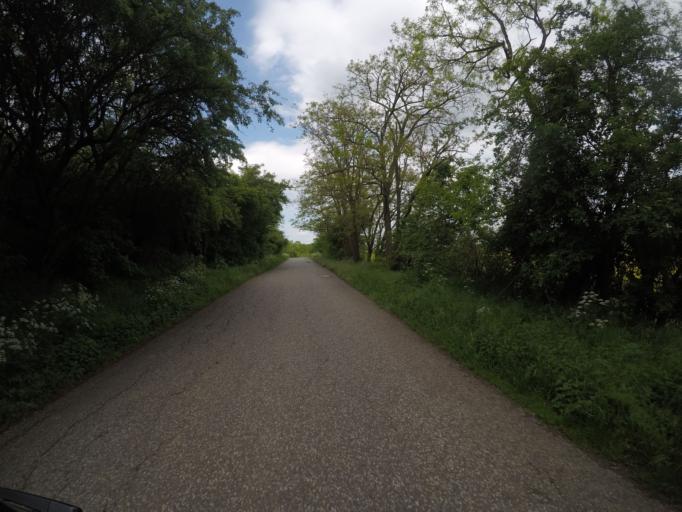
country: SK
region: Banskobystricky
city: Dudince
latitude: 48.0996
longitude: 18.8702
